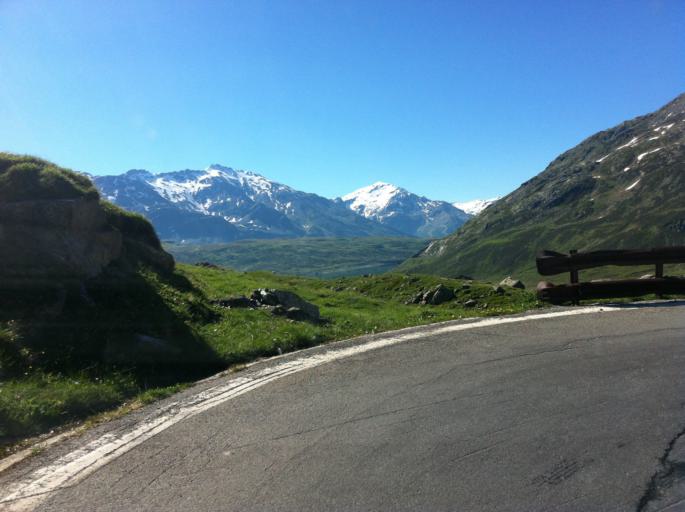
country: IT
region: Lombardy
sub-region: Provincia di Sondrio
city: Campodolcino
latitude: 46.5020
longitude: 9.3293
